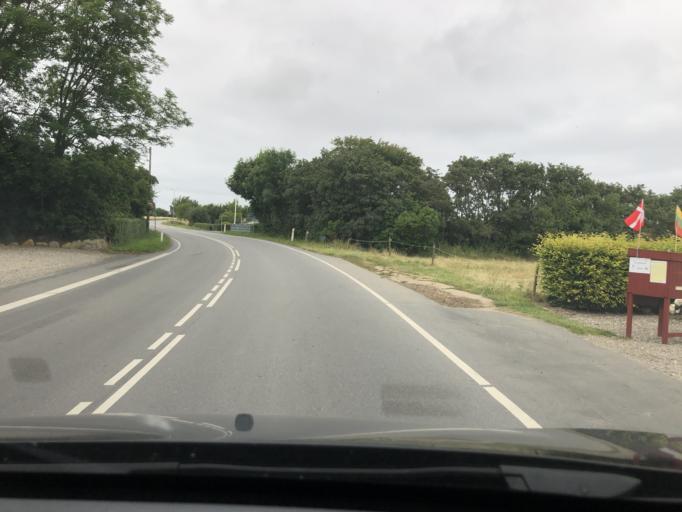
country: DK
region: South Denmark
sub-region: AEro Kommune
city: Marstal
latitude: 54.8491
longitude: 10.4978
